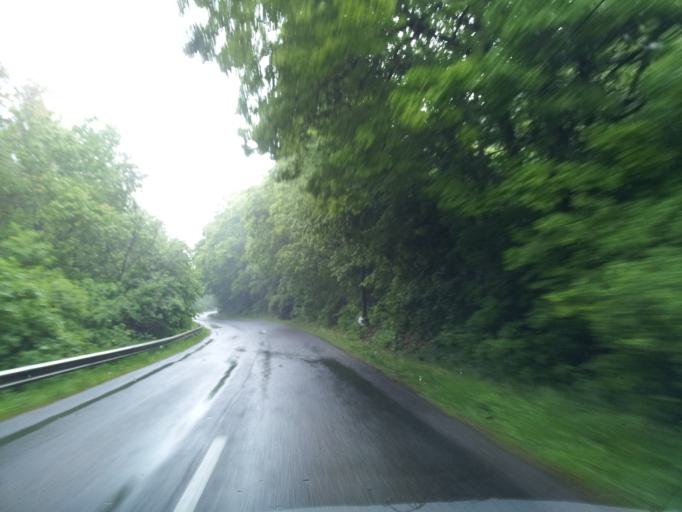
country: HU
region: Baranya
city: Hosszuheteny
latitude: 46.1762
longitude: 18.3229
